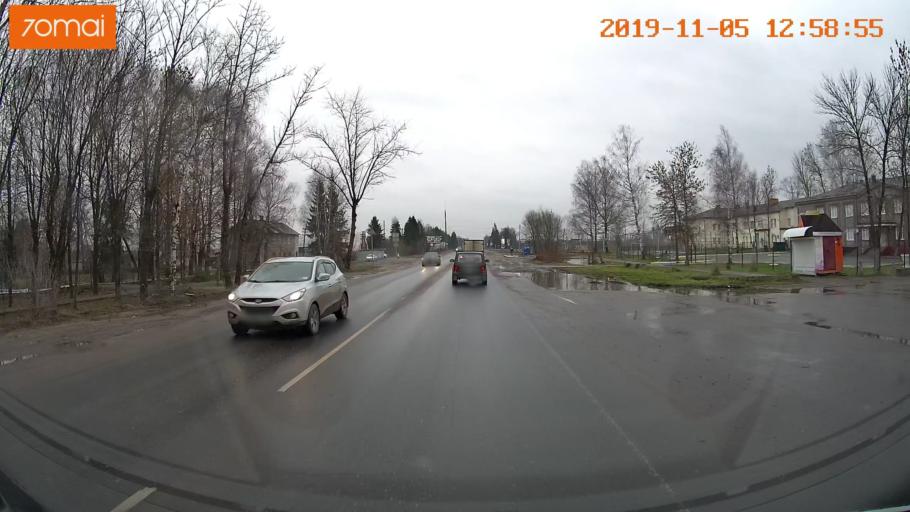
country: RU
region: Ivanovo
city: Kokhma
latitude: 56.9203
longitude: 41.1227
